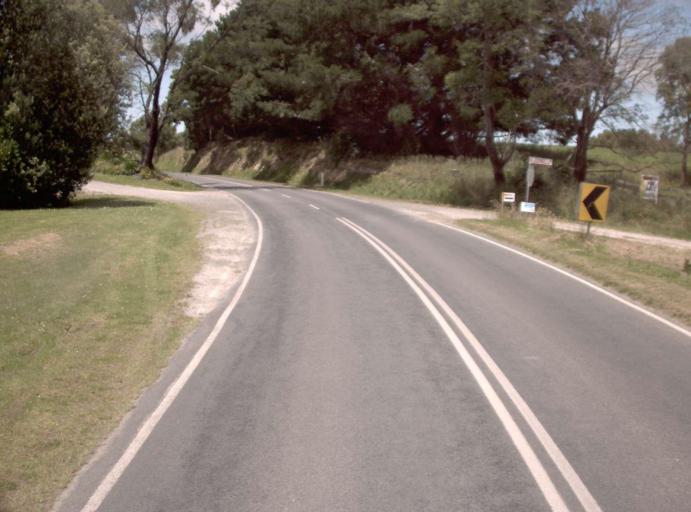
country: AU
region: Victoria
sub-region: Bass Coast
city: North Wonthaggi
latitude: -38.7099
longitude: 146.0895
